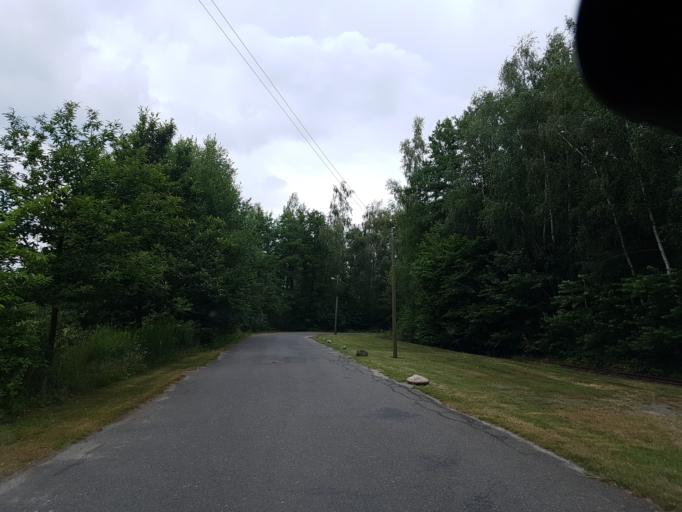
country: DE
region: Brandenburg
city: Sallgast
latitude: 51.5704
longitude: 13.8638
